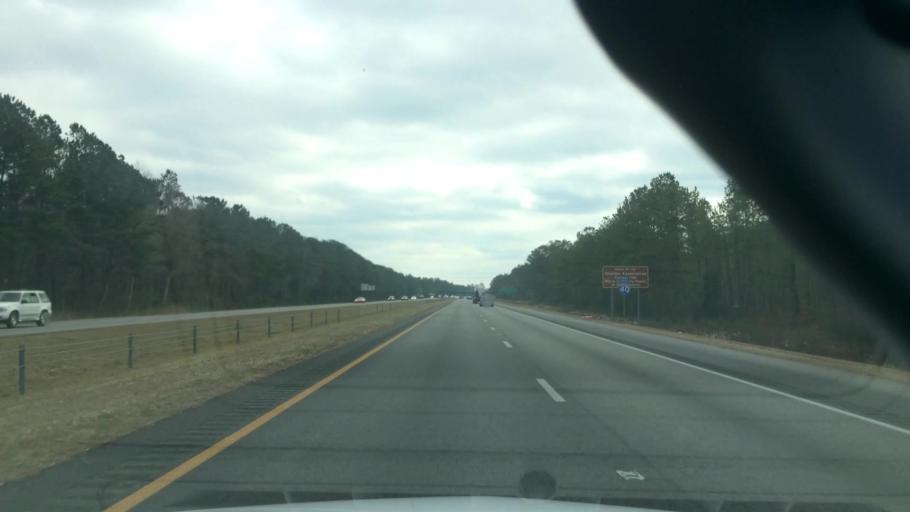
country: US
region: North Carolina
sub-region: New Hanover County
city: Skippers Corner
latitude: 34.3359
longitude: -77.8771
